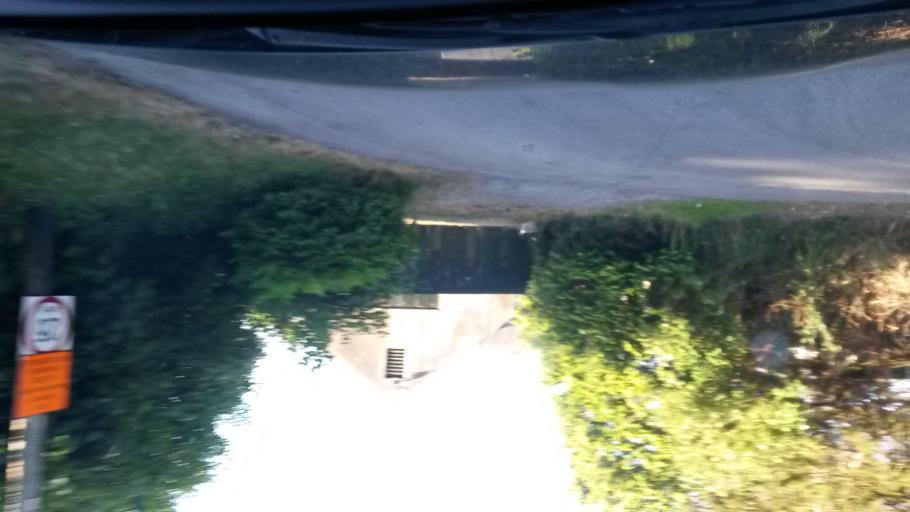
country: IE
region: Leinster
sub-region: Fingal County
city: Swords
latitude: 53.4905
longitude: -6.3053
